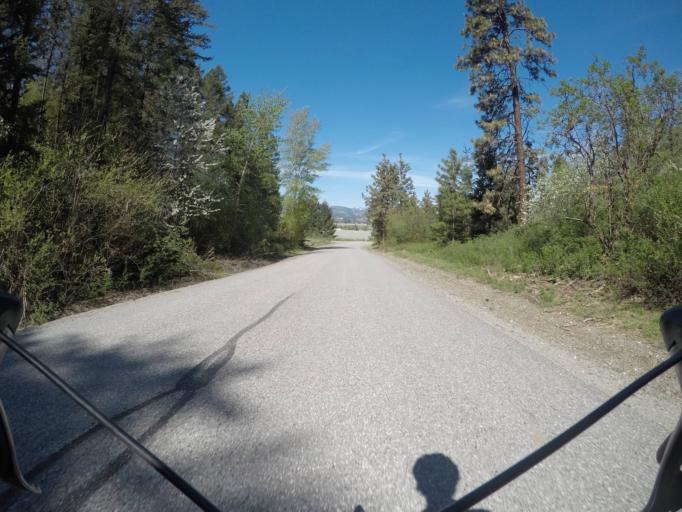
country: US
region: Washington
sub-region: Chelan County
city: Leavenworth
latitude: 47.5485
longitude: -120.5808
